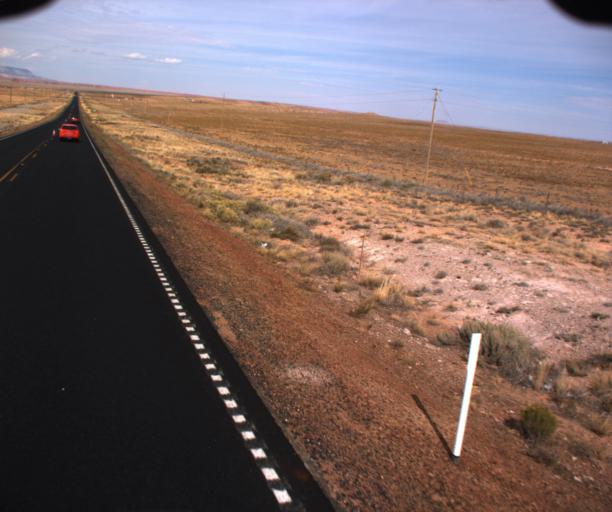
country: US
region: Arizona
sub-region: Apache County
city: Chinle
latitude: 36.0720
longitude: -109.6114
